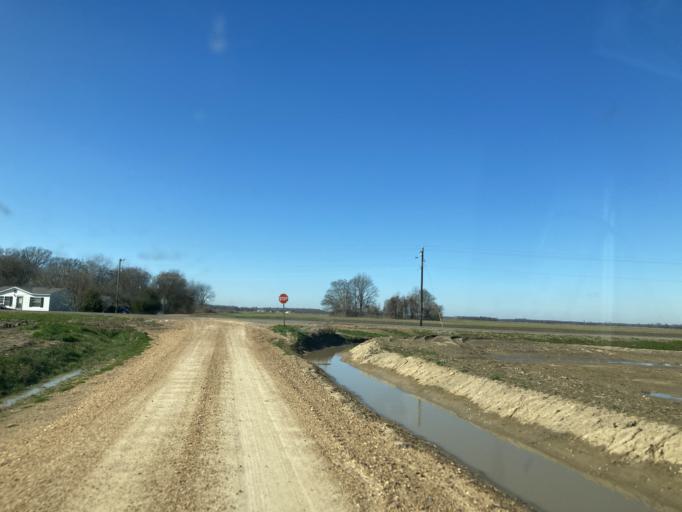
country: US
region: Mississippi
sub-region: Yazoo County
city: Yazoo City
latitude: 32.9703
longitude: -90.5949
